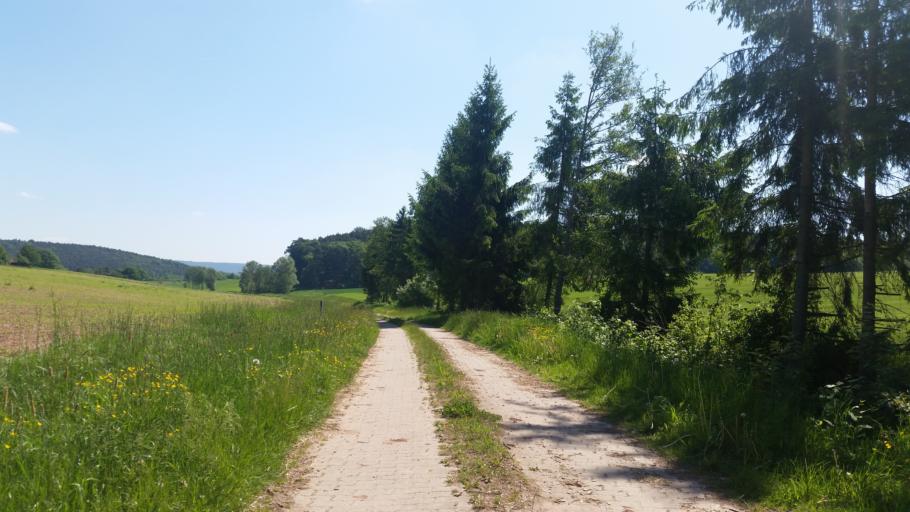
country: DE
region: Bavaria
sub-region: Regierungsbezirk Unterfranken
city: Burgpreppach
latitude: 50.1148
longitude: 10.6736
